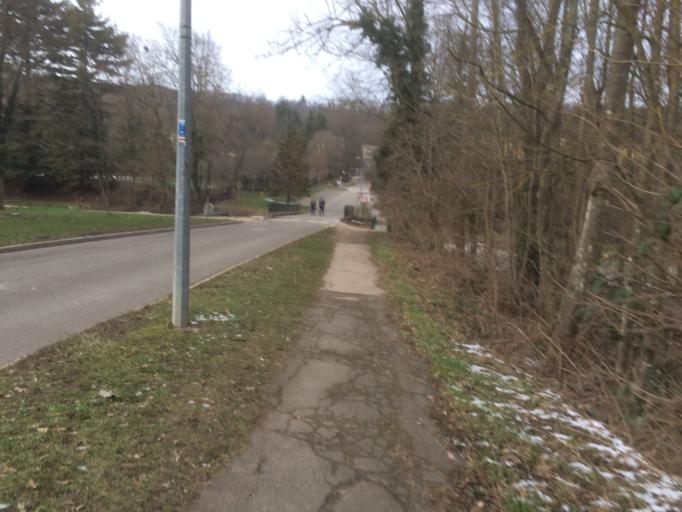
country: FR
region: Ile-de-France
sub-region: Departement de l'Essonne
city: Bures-sur-Yvette
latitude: 48.7005
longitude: 2.1734
